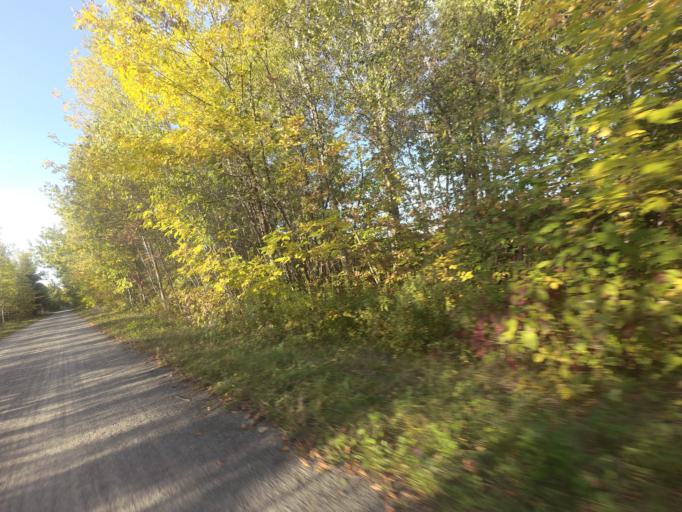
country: CA
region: Quebec
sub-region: Laurentides
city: Prevost
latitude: 45.8264
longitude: -74.0545
